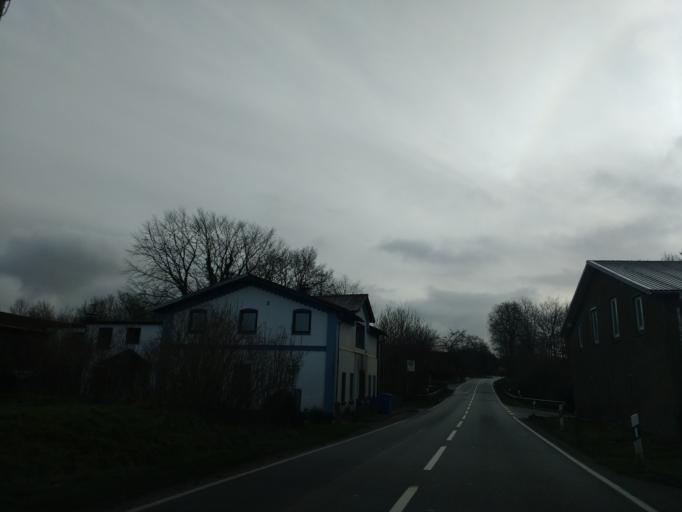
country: DE
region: Schleswig-Holstein
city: Damsdorf
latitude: 54.0584
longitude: 10.3319
